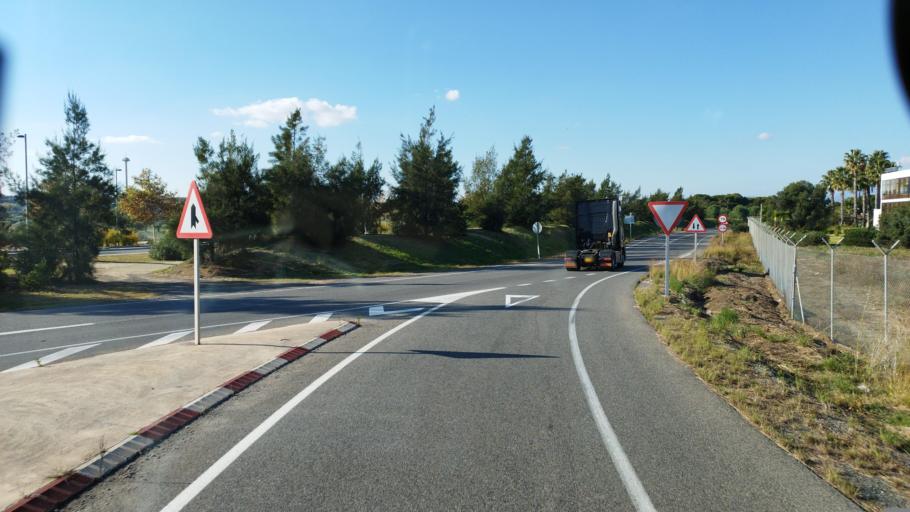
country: ES
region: Catalonia
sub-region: Provincia de Barcelona
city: La Pineda
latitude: 41.0939
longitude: 1.1755
